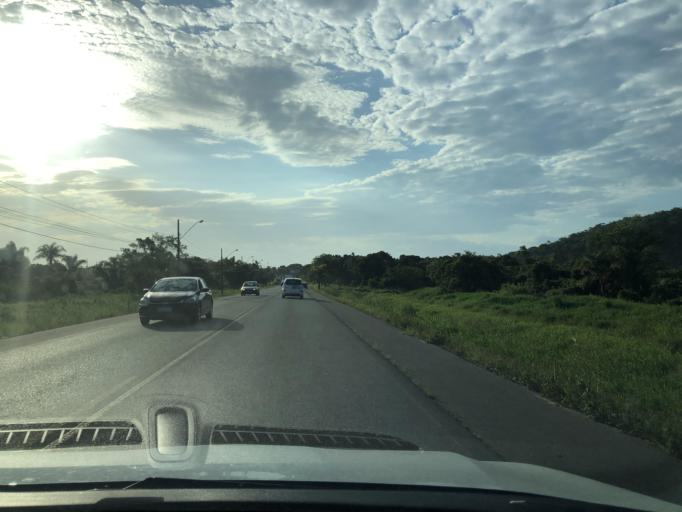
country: BR
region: Santa Catarina
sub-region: Sao Francisco Do Sul
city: Sao Francisco do Sul
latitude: -26.2059
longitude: -48.5331
